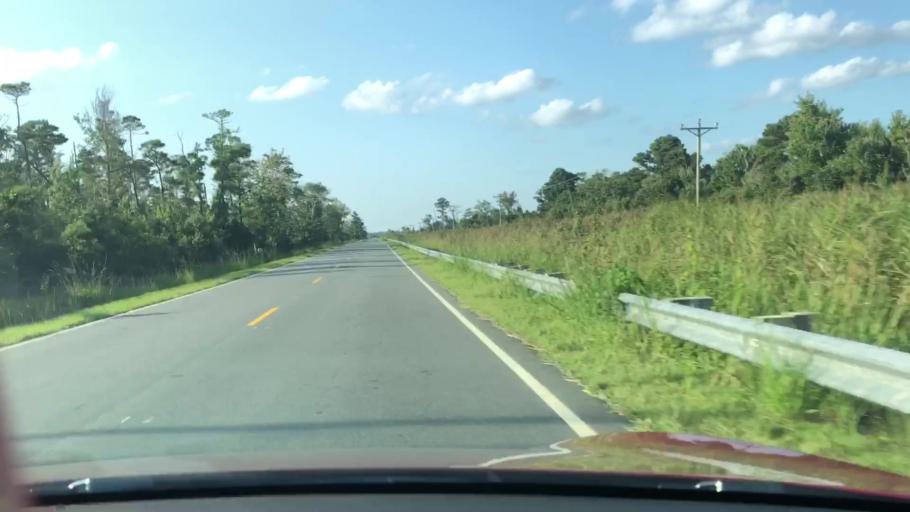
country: US
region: North Carolina
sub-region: Dare County
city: Wanchese
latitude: 35.6751
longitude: -75.7792
